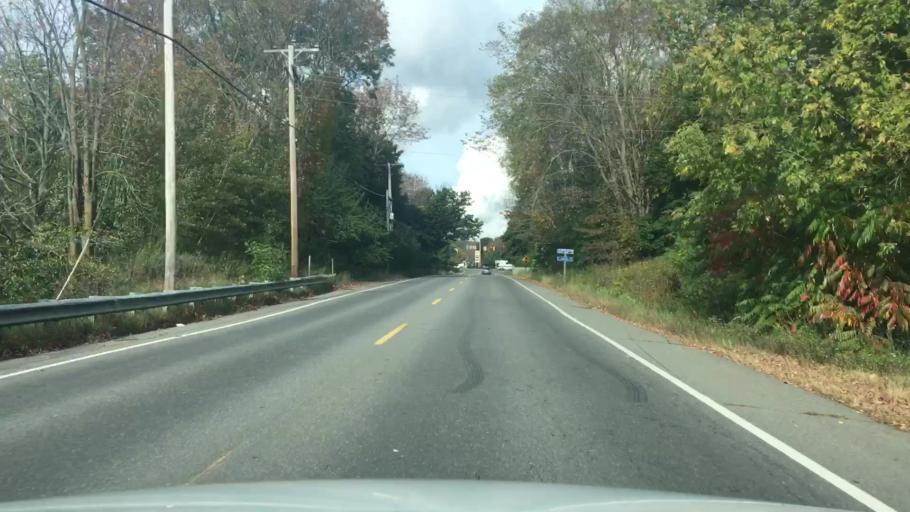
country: US
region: Maine
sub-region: Knox County
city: Rockland
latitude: 44.1221
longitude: -69.1152
